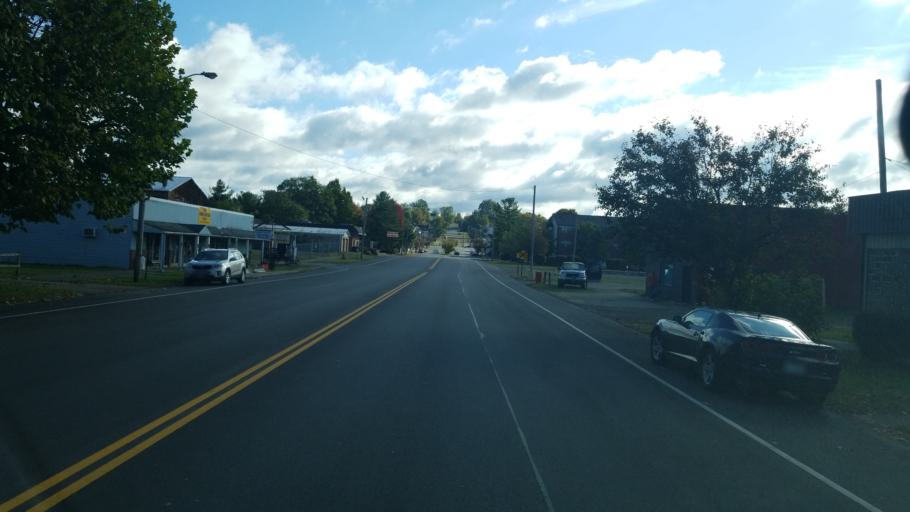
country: US
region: Ohio
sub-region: Jackson County
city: Wellston
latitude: 39.1238
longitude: -82.5380
